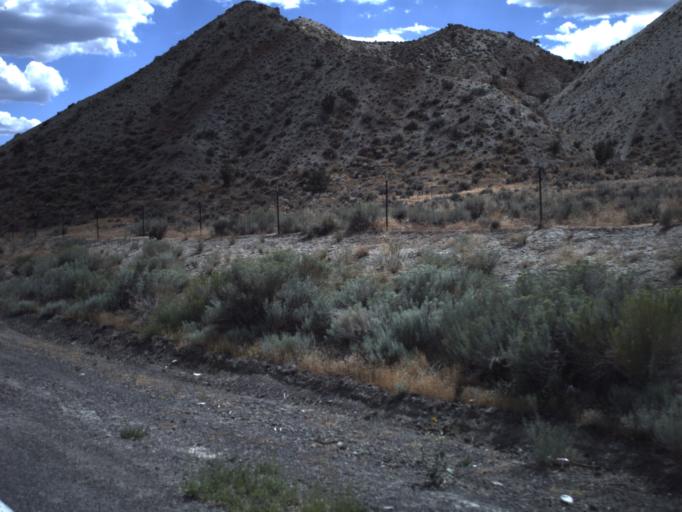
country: US
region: Utah
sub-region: Sanpete County
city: Gunnison
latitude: 39.1404
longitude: -111.7323
